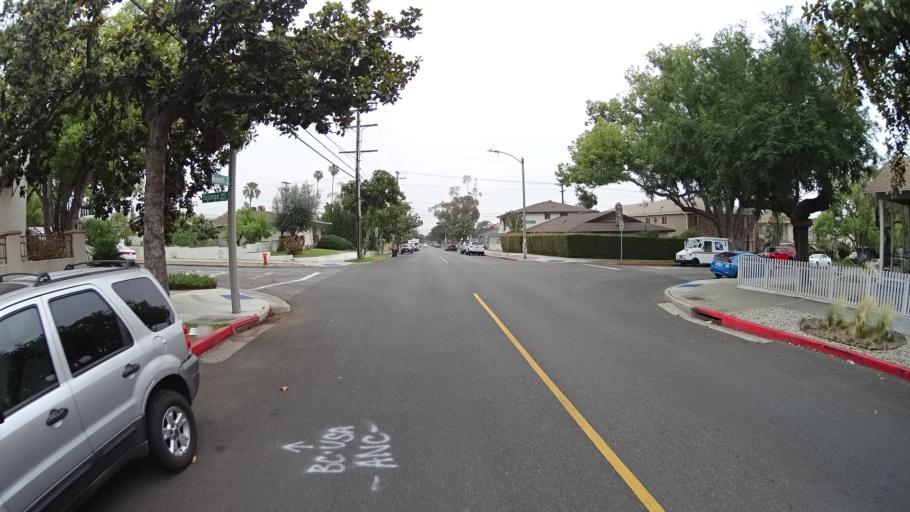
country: US
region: California
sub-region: Los Angeles County
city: Burbank
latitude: 34.1864
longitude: -118.2995
